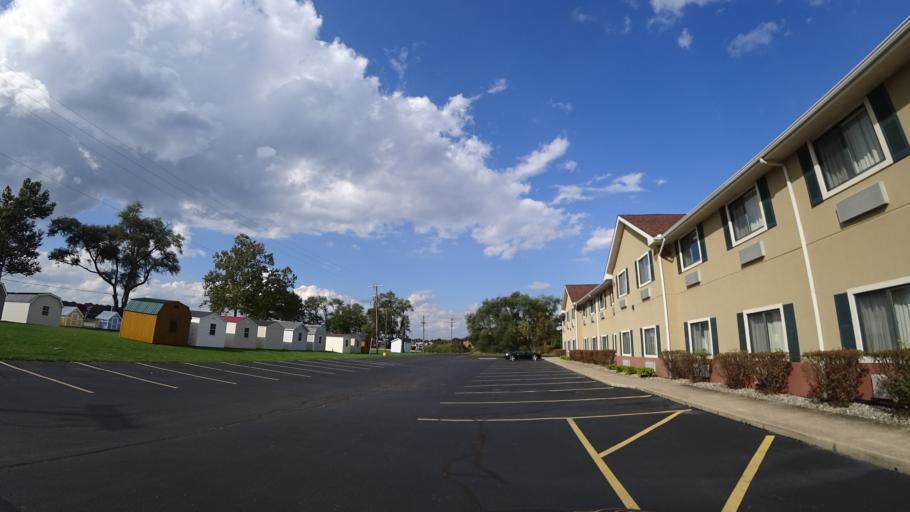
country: US
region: Michigan
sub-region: Saint Joseph County
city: Three Rivers
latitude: 41.9352
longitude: -85.6503
